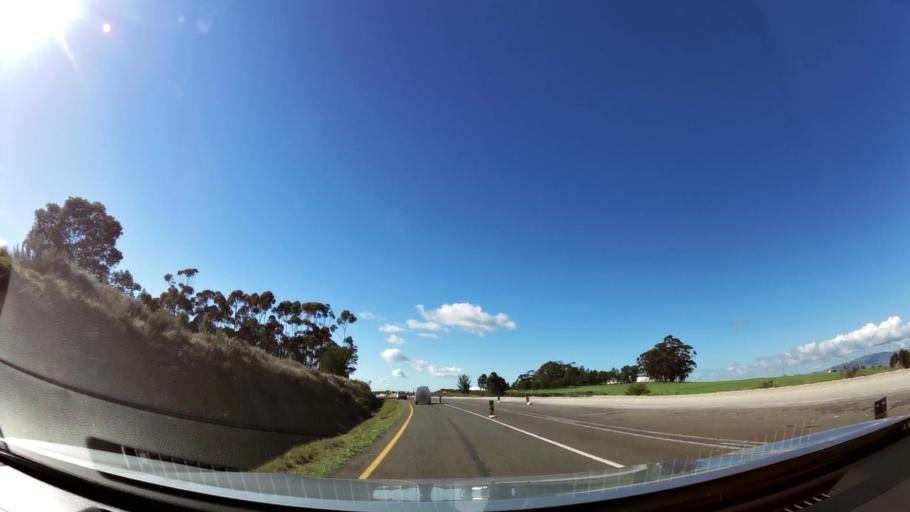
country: ZA
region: Western Cape
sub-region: Overberg District Municipality
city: Caledon
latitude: -34.2074
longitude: 19.5833
